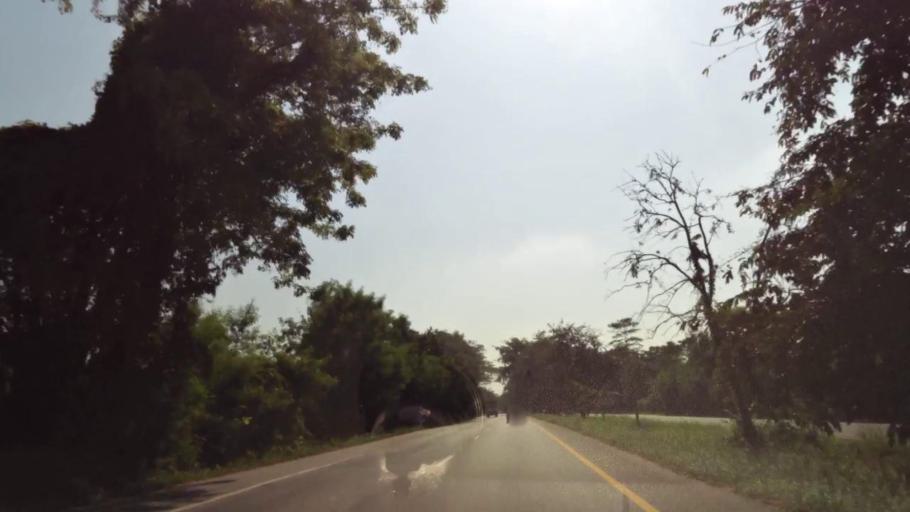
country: TH
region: Phichit
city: Bueng Na Rang
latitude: 16.0243
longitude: 100.1147
